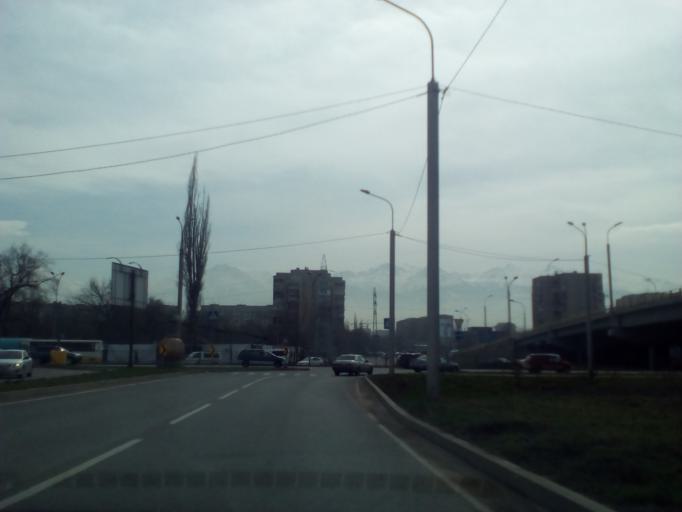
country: KZ
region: Almaty Qalasy
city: Almaty
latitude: 43.2442
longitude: 76.8282
